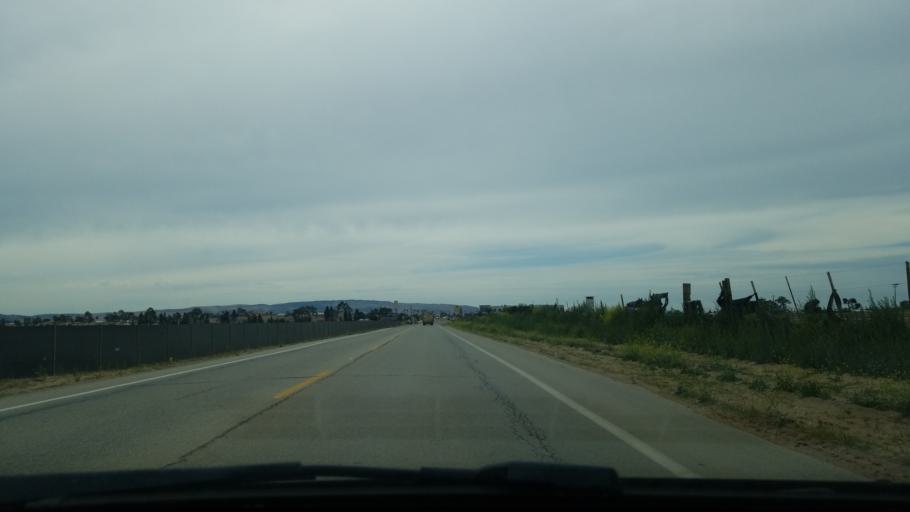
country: US
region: California
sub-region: Santa Barbara County
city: Santa Maria
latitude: 34.9238
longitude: -120.4107
